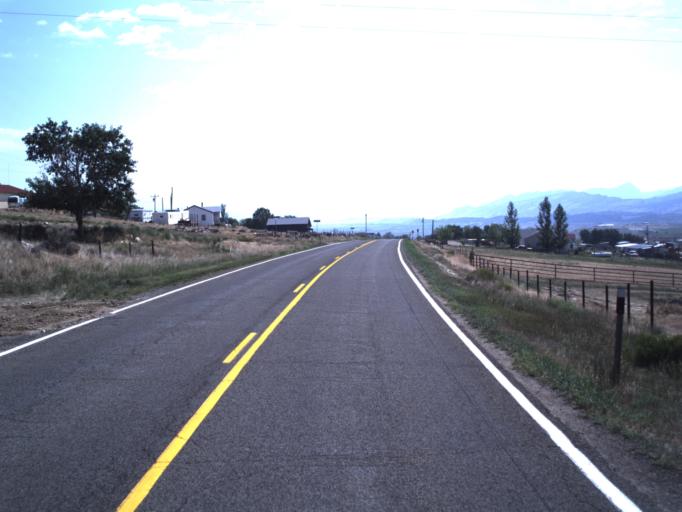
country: US
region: Utah
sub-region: Daggett County
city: Manila
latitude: 40.9772
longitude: -109.7561
